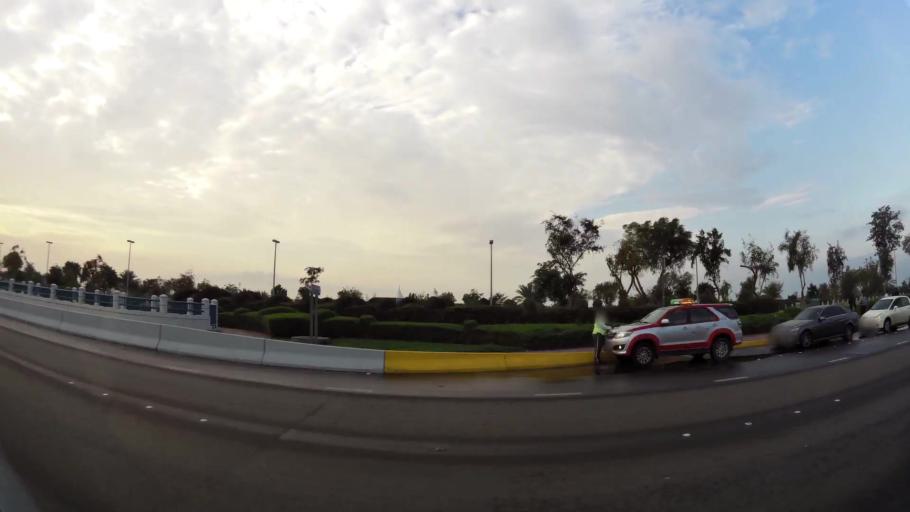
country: AE
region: Abu Dhabi
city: Abu Dhabi
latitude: 24.4096
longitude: 54.4633
